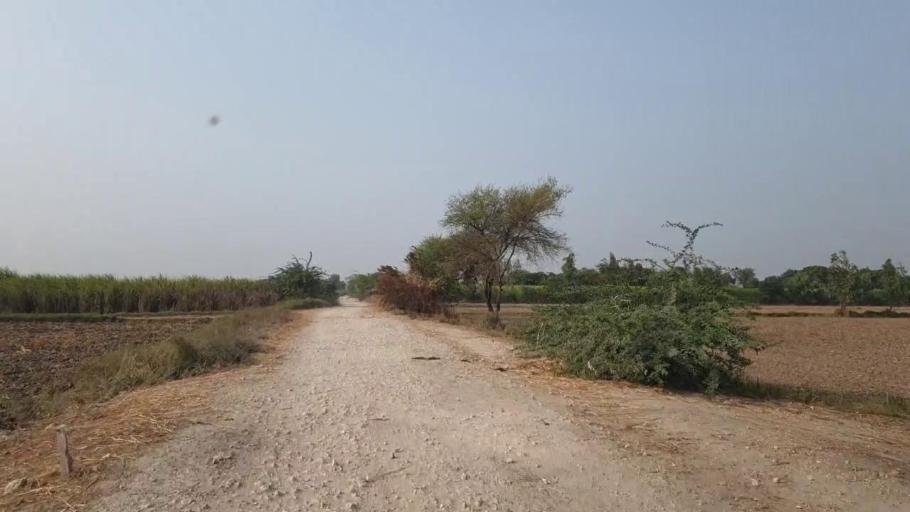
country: PK
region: Sindh
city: Tando Muhammad Khan
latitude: 25.0791
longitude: 68.5893
